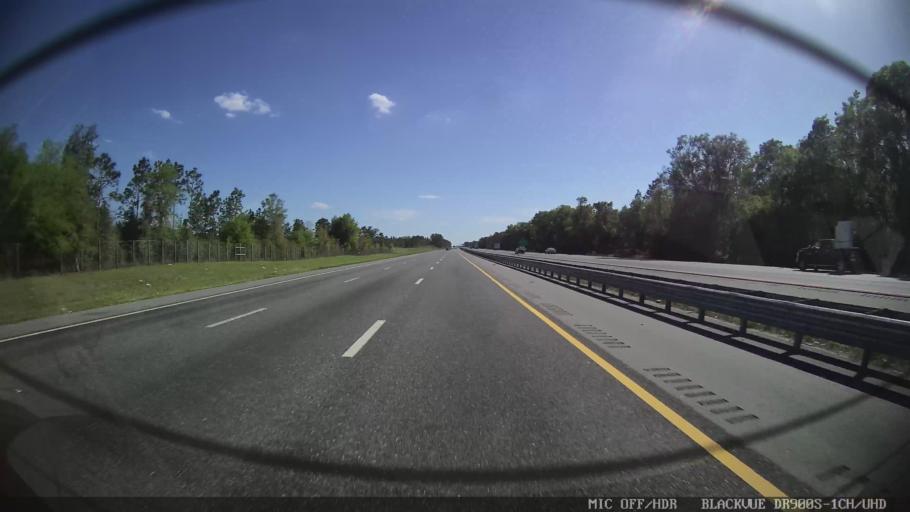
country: US
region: Florida
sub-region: Hernando County
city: Hill 'n Dale
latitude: 28.5537
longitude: -82.2363
